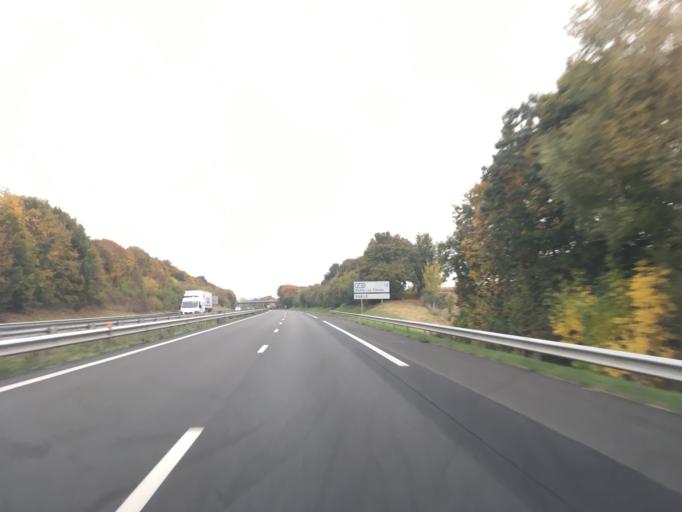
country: FR
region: Pays de la Loire
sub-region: Departement de Maine-et-Loire
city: Durtal
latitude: 47.6767
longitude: -0.2556
